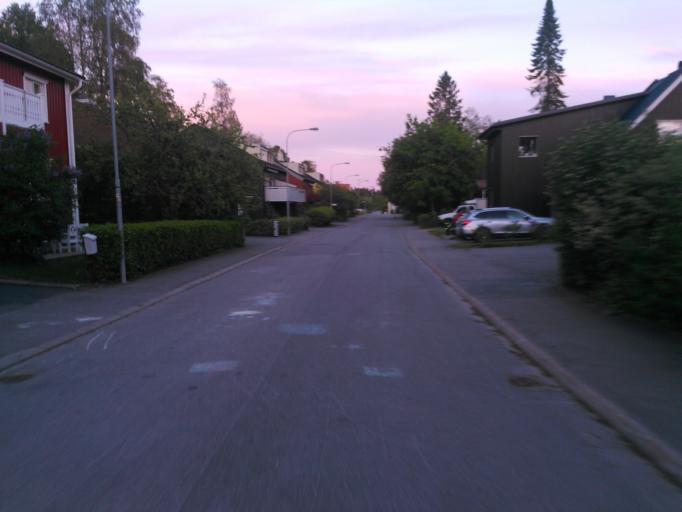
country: SE
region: Vaesterbotten
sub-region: Umea Kommun
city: Umea
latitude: 63.8089
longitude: 20.2982
